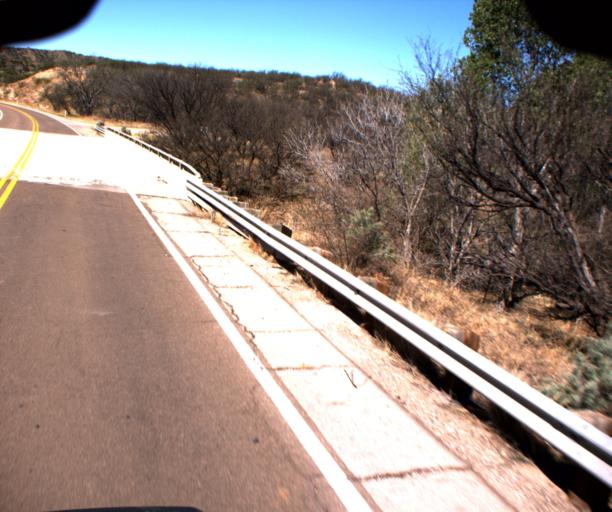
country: US
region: Arizona
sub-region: Pima County
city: Corona de Tucson
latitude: 31.6547
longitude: -110.7115
